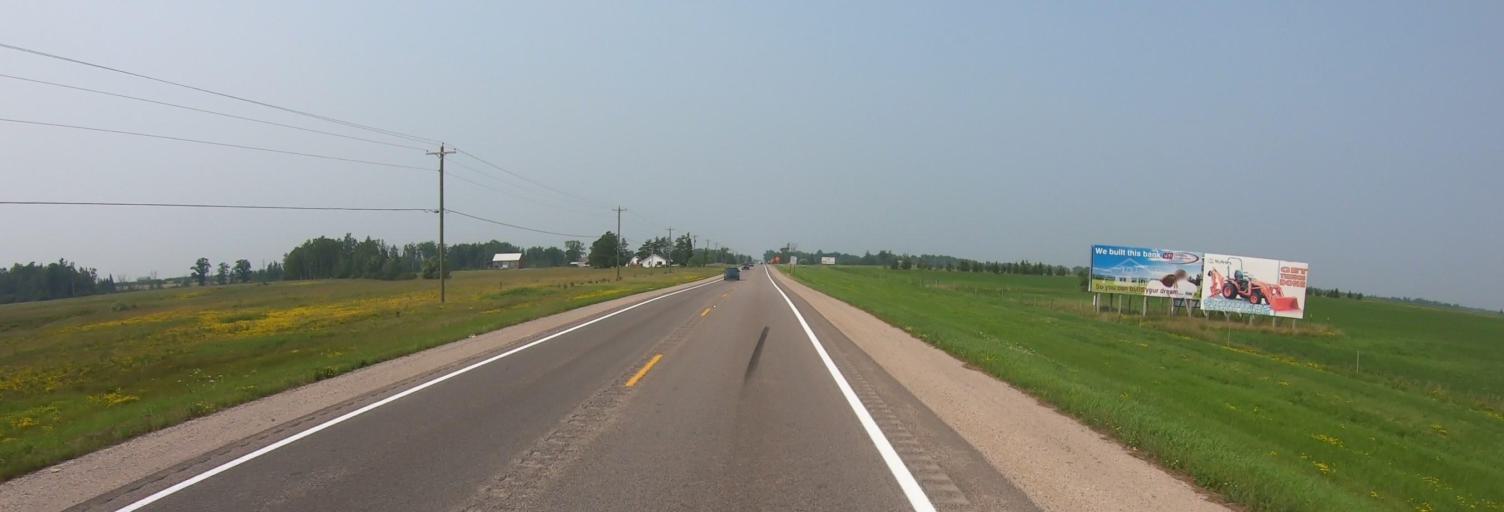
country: US
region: Michigan
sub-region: Chippewa County
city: Sault Ste. Marie
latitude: 46.1340
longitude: -84.3633
